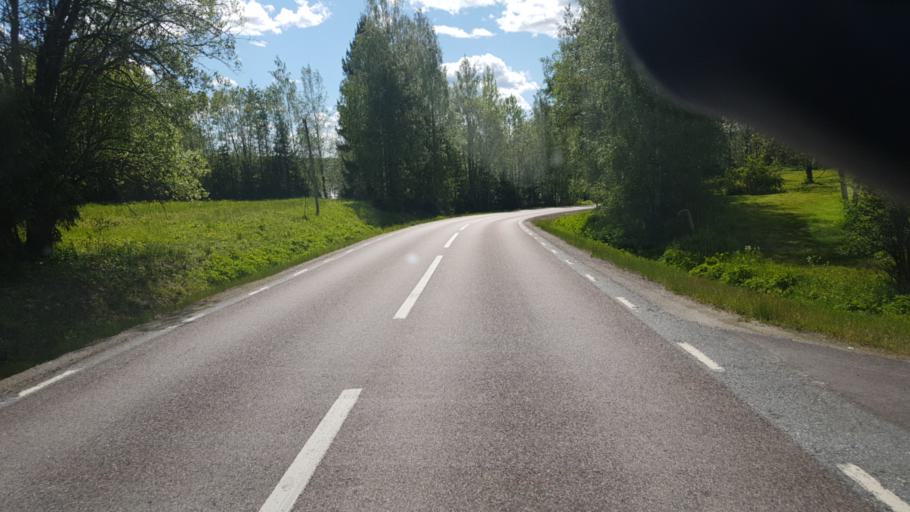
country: SE
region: Vaermland
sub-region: Sunne Kommun
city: Sunne
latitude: 59.6748
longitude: 13.0296
